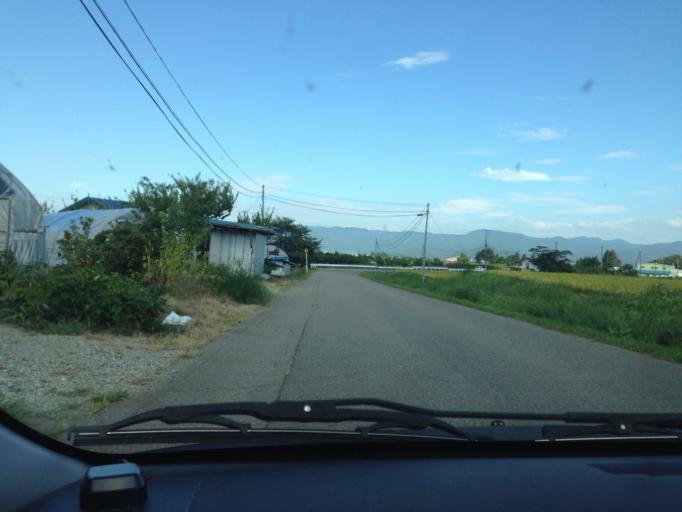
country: JP
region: Fukushima
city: Kitakata
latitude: 37.4507
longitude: 139.8233
